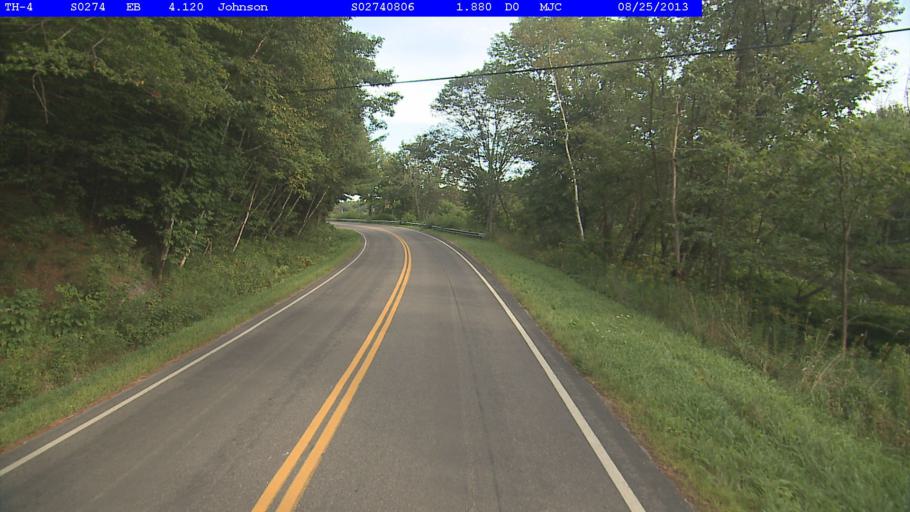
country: US
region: Vermont
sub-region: Lamoille County
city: Johnson
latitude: 44.6454
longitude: -72.7192
